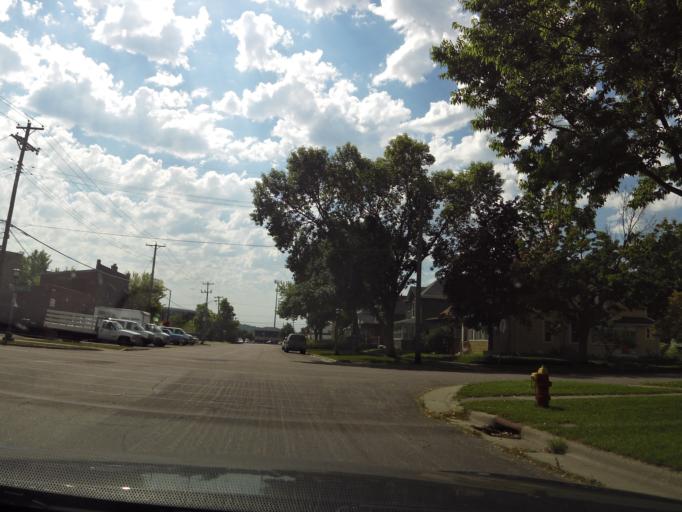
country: US
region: Minnesota
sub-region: Dakota County
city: West Saint Paul
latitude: 44.9293
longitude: -93.1258
